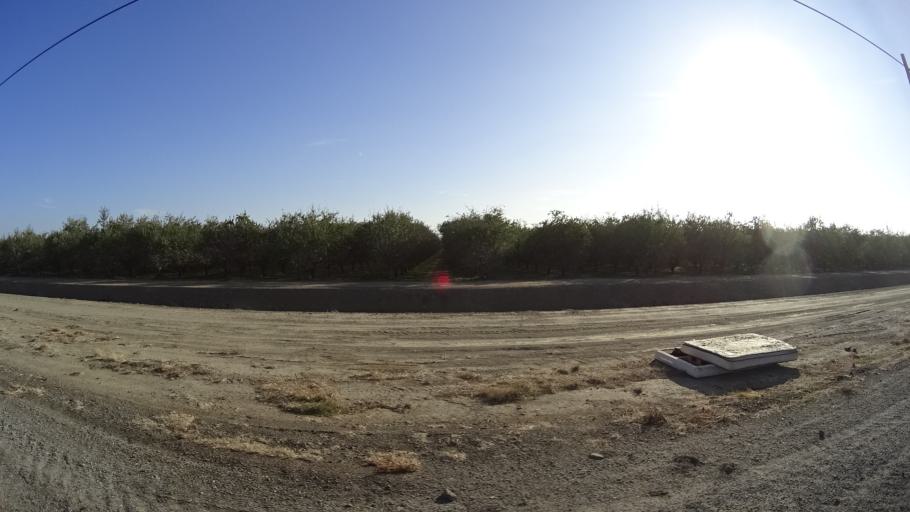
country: US
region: California
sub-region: Kern County
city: Rosedale
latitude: 35.2962
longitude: -119.1578
